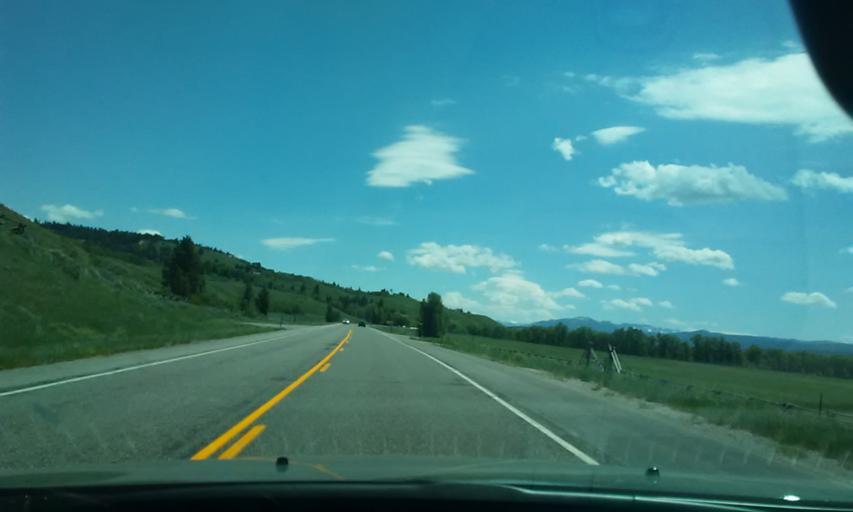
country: US
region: Wyoming
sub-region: Teton County
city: Jackson
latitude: 43.8392
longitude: -110.4671
